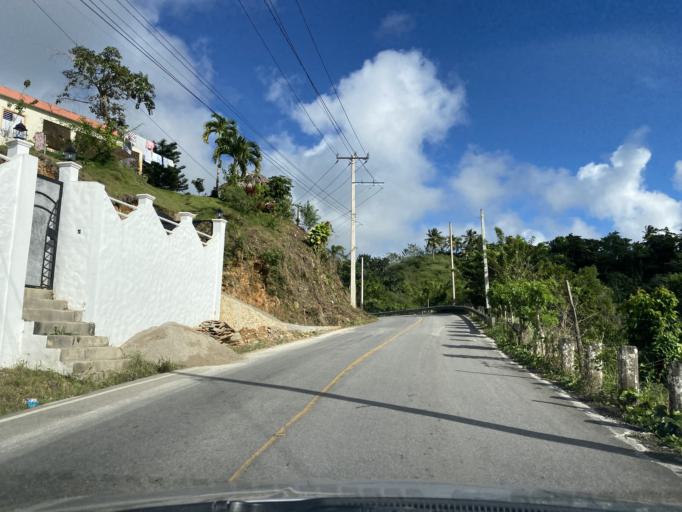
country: DO
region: Samana
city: Las Terrenas
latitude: 19.2613
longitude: -69.5683
